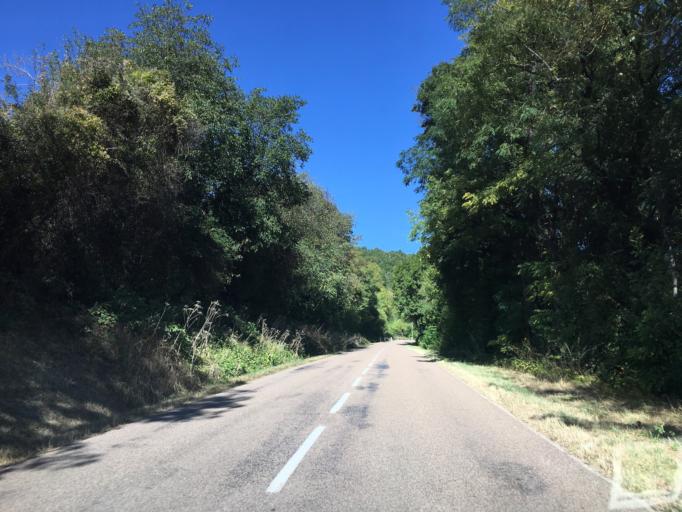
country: FR
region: Bourgogne
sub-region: Departement de l'Yonne
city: Vermenton
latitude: 47.6326
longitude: 3.6584
